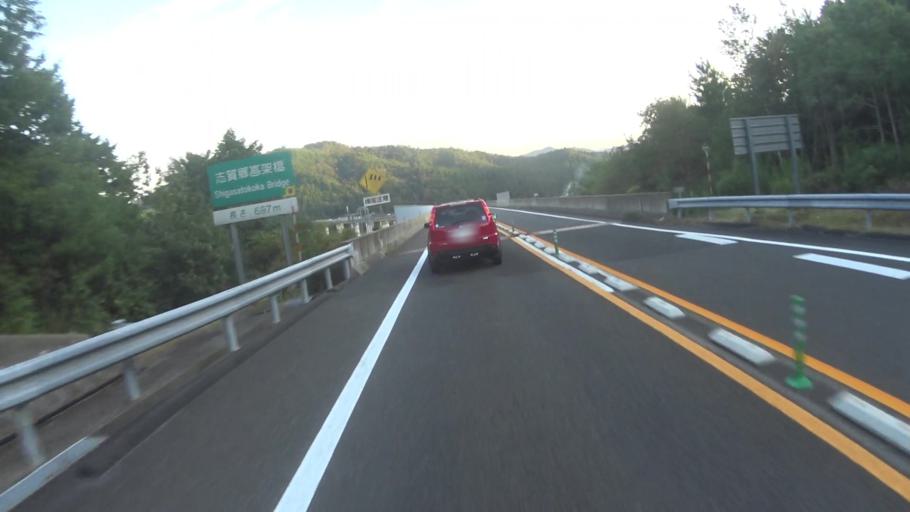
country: JP
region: Kyoto
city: Ayabe
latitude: 35.3893
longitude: 135.2409
